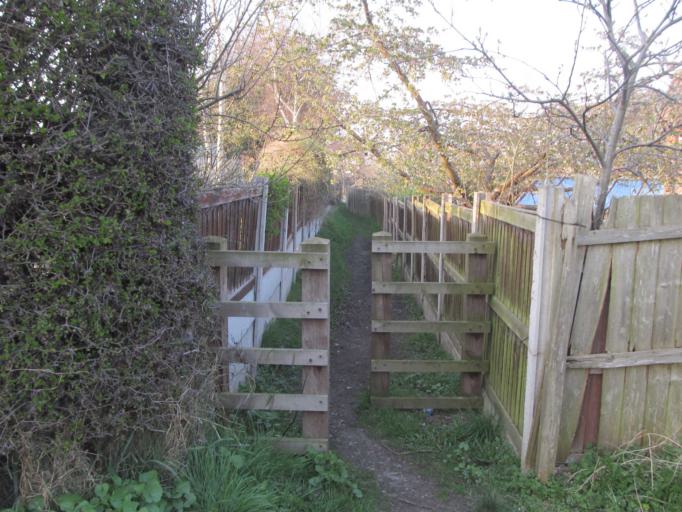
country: GB
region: Wales
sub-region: County of Flintshire
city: Buckley
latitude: 53.2023
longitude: -3.0917
